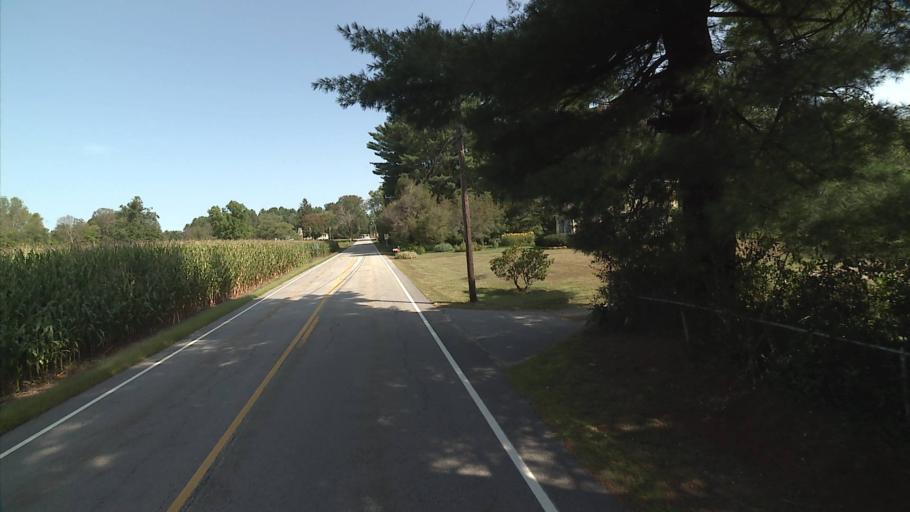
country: US
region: Connecticut
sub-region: Windham County
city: Wauregan
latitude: 41.7663
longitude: -71.9562
